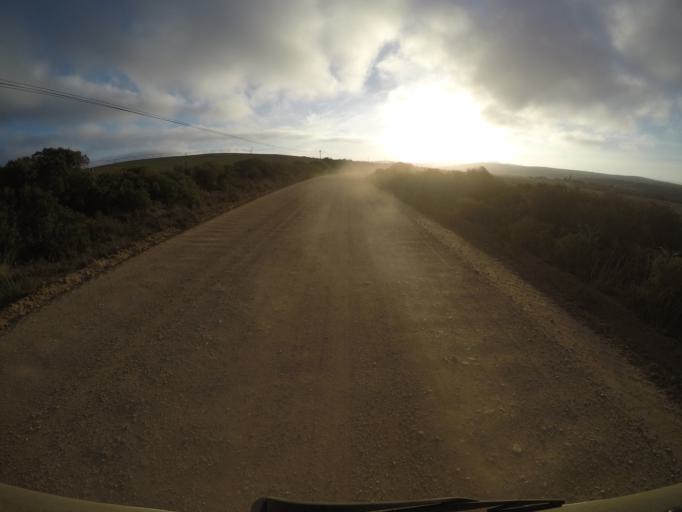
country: ZA
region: Western Cape
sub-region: Eden District Municipality
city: Mossel Bay
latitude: -34.1085
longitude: 22.0663
